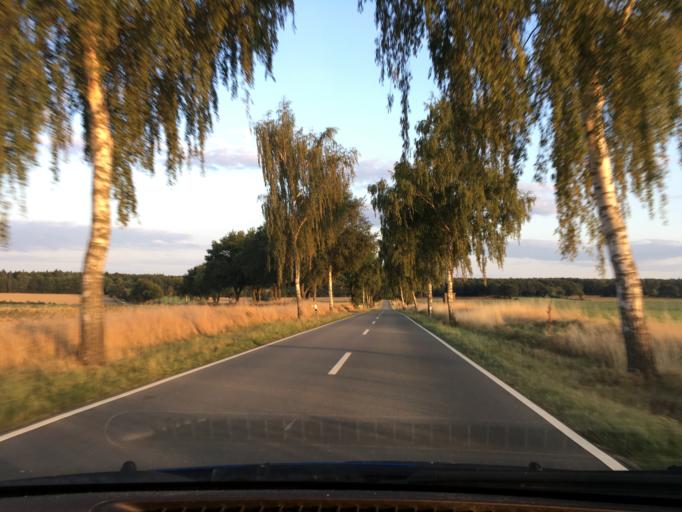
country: DE
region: Lower Saxony
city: Tosterglope
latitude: 53.2385
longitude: 10.7908
